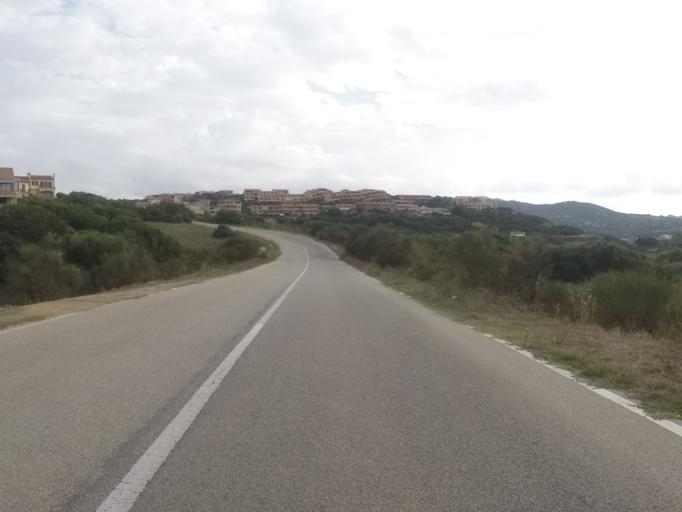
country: IT
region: Sardinia
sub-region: Provincia di Olbia-Tempio
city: Palau
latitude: 41.1822
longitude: 9.3763
